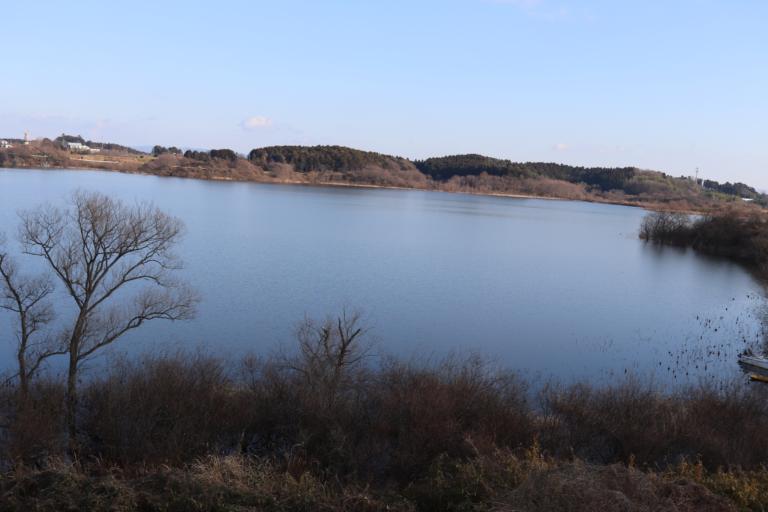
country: JP
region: Miyagi
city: Wakuya
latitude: 38.6876
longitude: 141.1188
